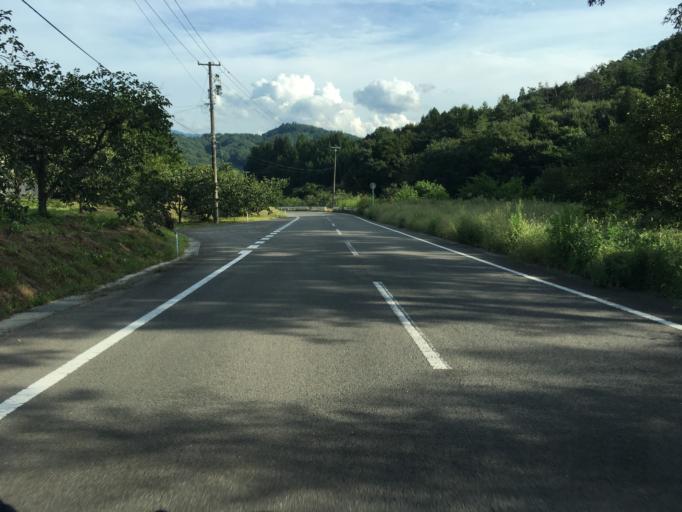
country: JP
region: Fukushima
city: Hobaramachi
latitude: 37.7980
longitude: 140.5912
